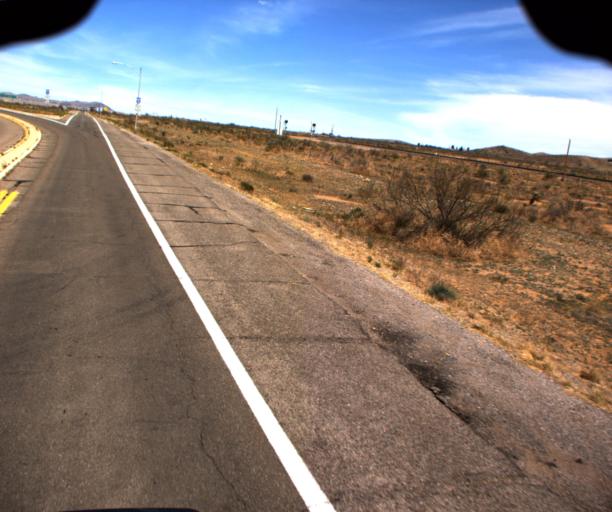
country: US
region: Arizona
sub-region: Cochise County
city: Willcox
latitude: 32.3030
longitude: -109.7974
